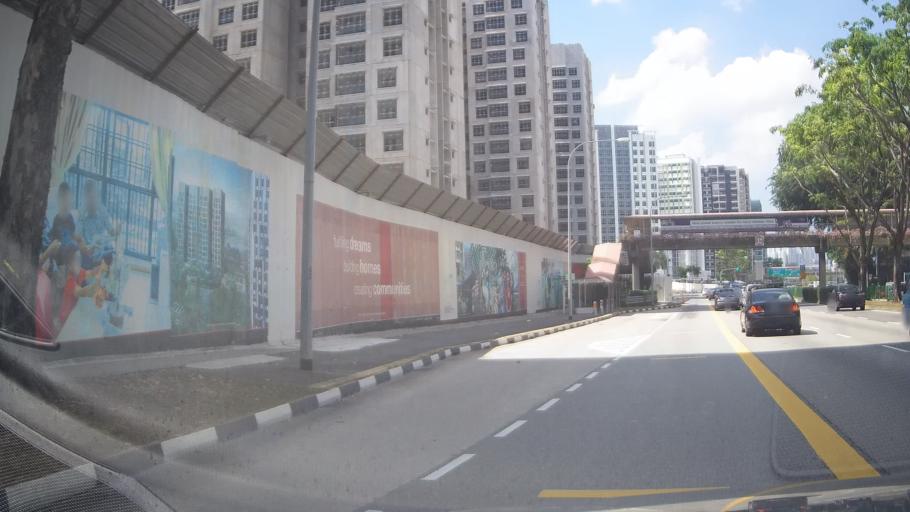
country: SG
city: Singapore
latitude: 1.3368
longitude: 103.8708
